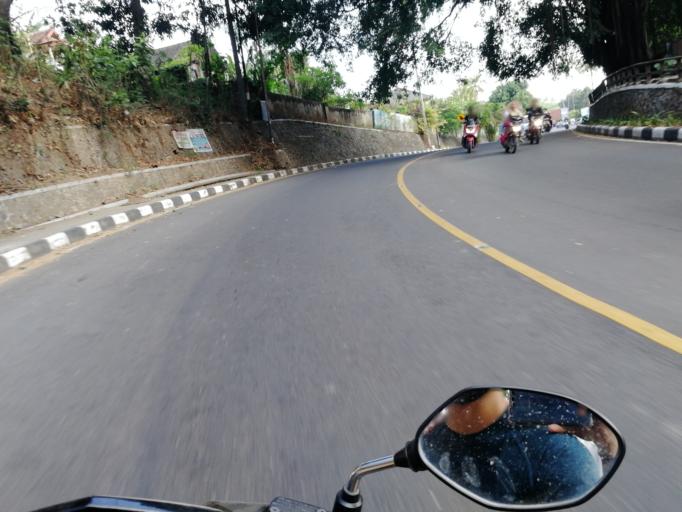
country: ID
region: West Nusa Tenggara
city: Mambalan
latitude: -8.4945
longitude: 116.0447
